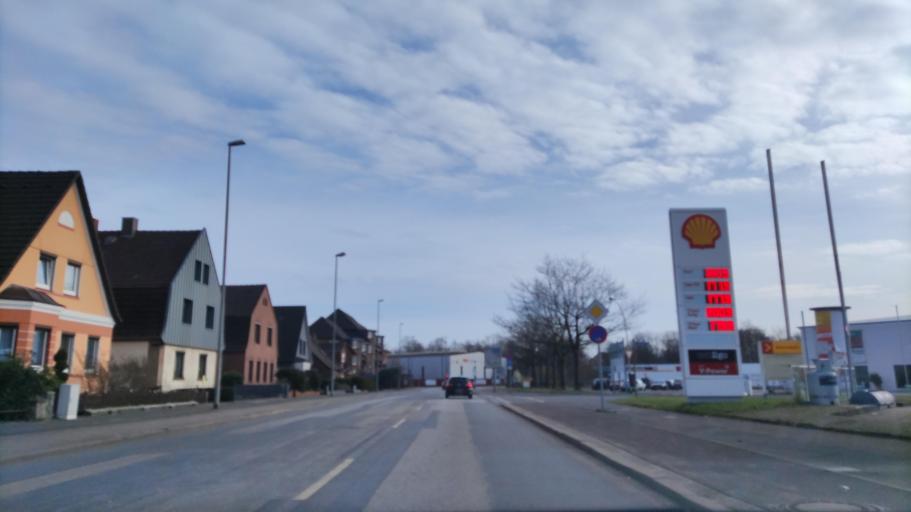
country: DE
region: Schleswig-Holstein
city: Neumunster
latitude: 54.0856
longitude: 9.9936
